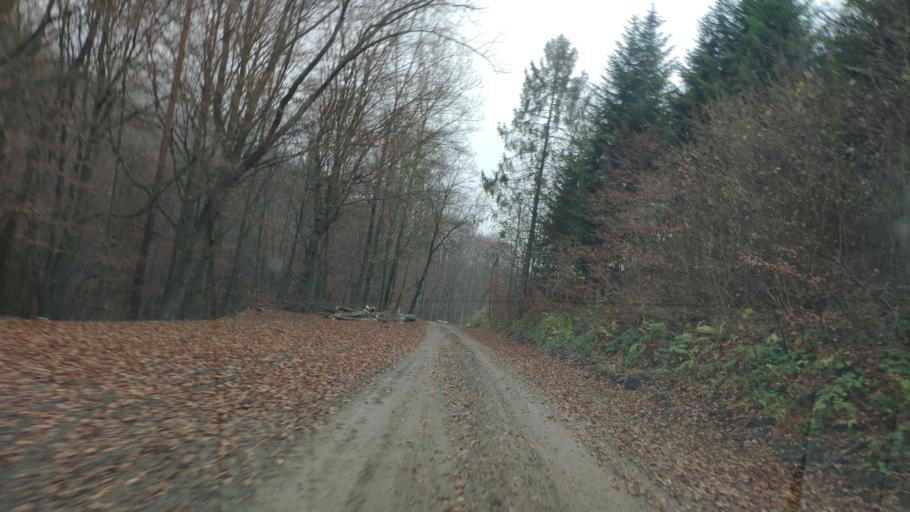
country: SK
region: Presovsky
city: Sabinov
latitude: 49.1512
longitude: 21.2049
